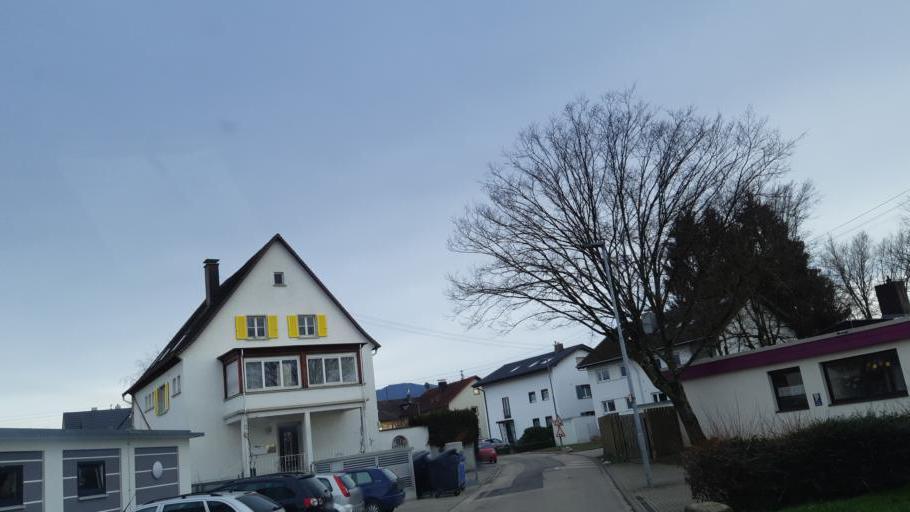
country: DE
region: Baden-Wuerttemberg
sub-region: Freiburg Region
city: Emmendingen
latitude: 48.1009
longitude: 7.8772
